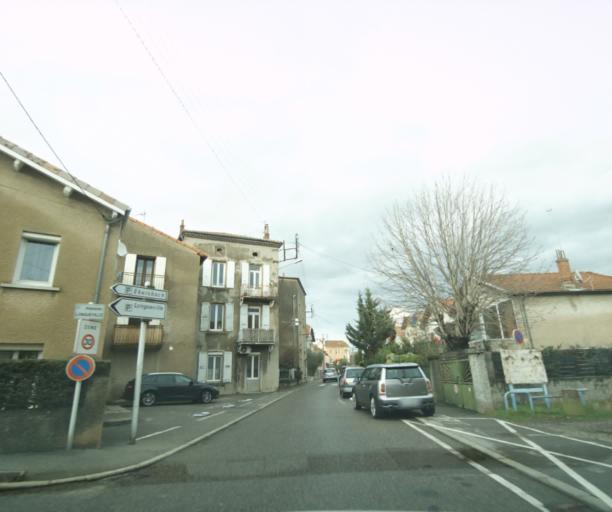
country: FR
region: Rhone-Alpes
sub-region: Departement de la Drome
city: Valence
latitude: 44.9434
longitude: 4.8954
